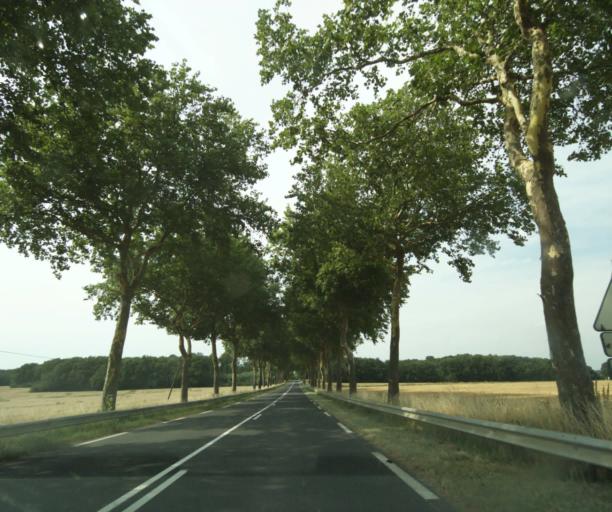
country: FR
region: Centre
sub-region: Departement d'Indre-et-Loire
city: Neuille-Pont-Pierre
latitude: 47.5742
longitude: 0.5449
